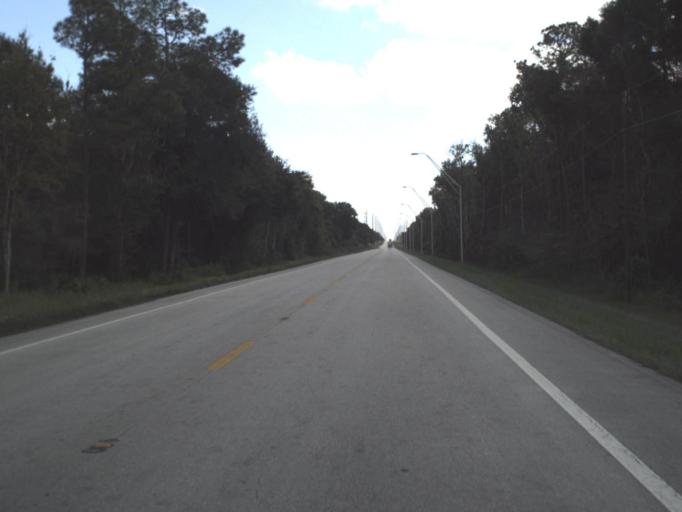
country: US
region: Florida
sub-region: Highlands County
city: Sebring
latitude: 27.4123
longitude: -81.5228
